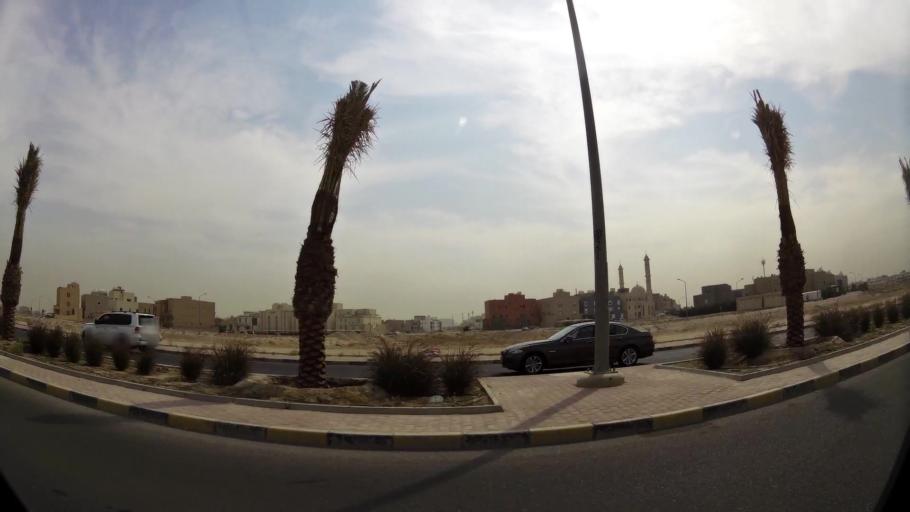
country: KW
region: Al Farwaniyah
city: Janub as Surrah
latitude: 29.2967
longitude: 47.9935
